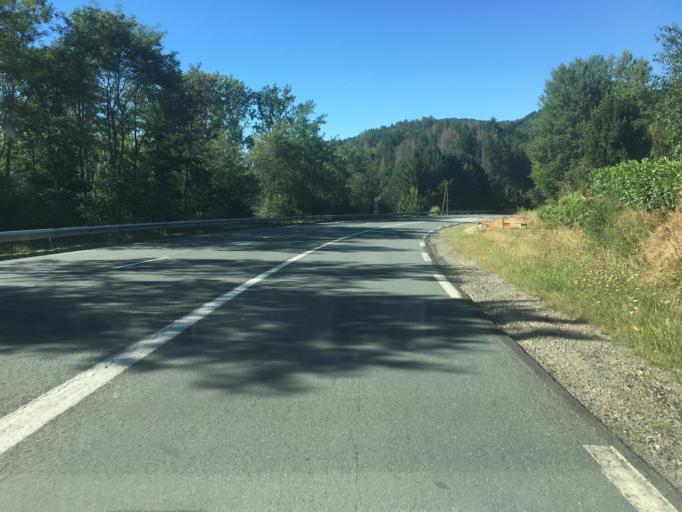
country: FR
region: Limousin
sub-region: Departement de la Correze
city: Bort-les-Orgues
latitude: 45.4209
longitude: 2.5034
